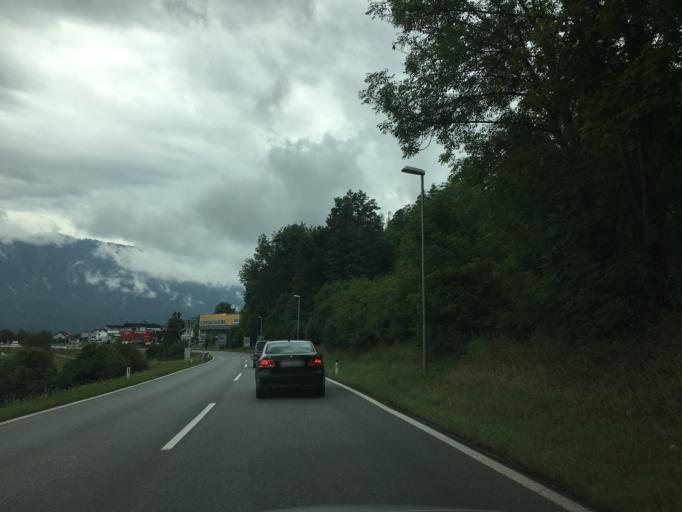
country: AT
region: Tyrol
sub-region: Politischer Bezirk Imst
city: Imst
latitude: 47.2510
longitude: 10.7465
